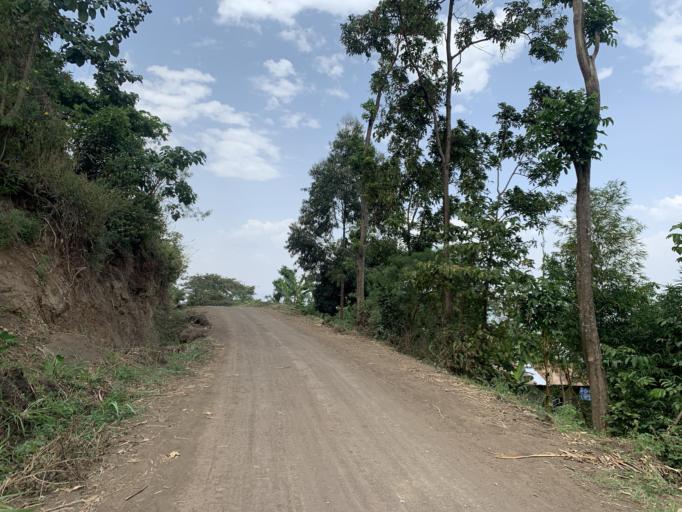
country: UG
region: Eastern Region
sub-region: Sironko District
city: Sironko
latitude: 1.2610
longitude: 34.3035
